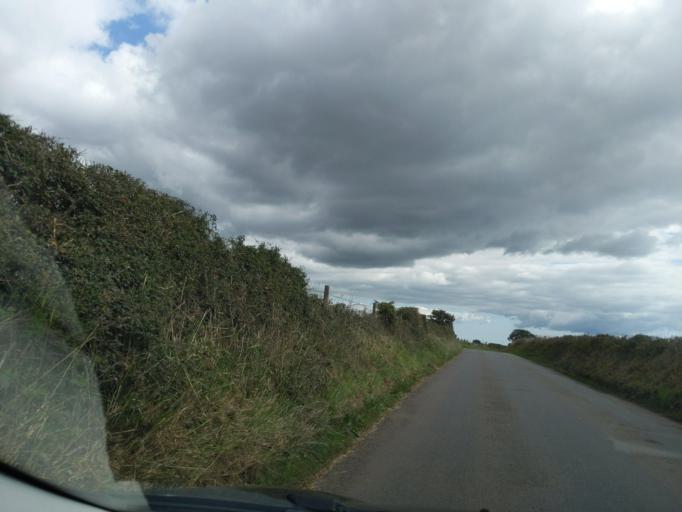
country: GB
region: England
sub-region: Plymouth
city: Plymstock
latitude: 50.3442
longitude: -4.0991
